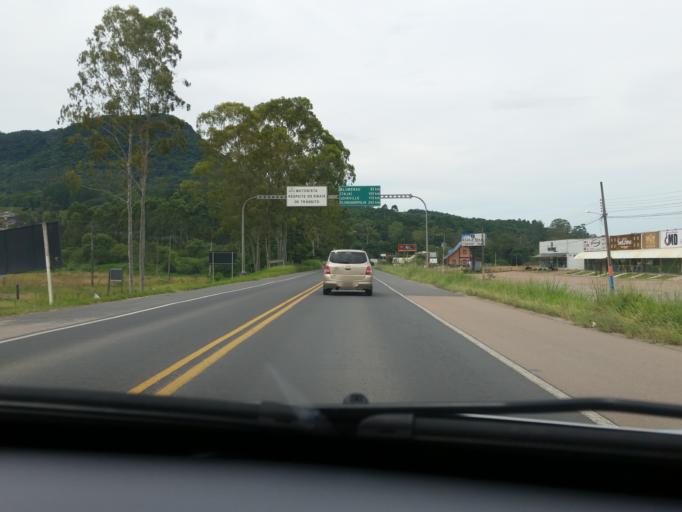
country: BR
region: Santa Catarina
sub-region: Rio Do Sul
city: Rio do Sul
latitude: -27.1929
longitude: -49.6228
